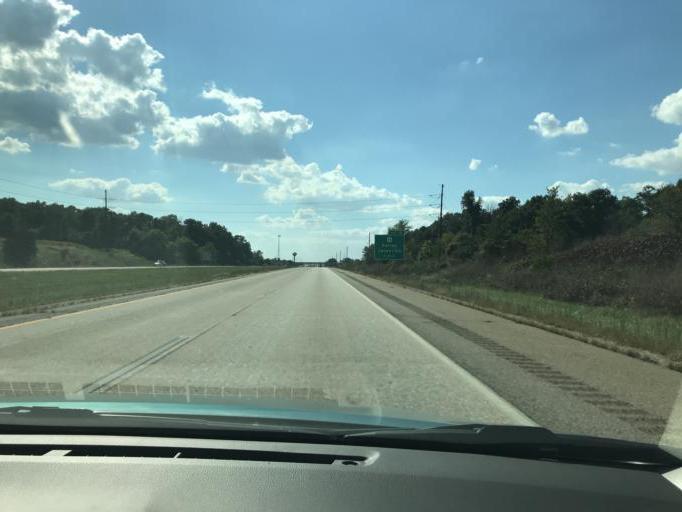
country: US
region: Wisconsin
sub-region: Walworth County
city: Darien
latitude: 42.6166
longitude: -88.6955
